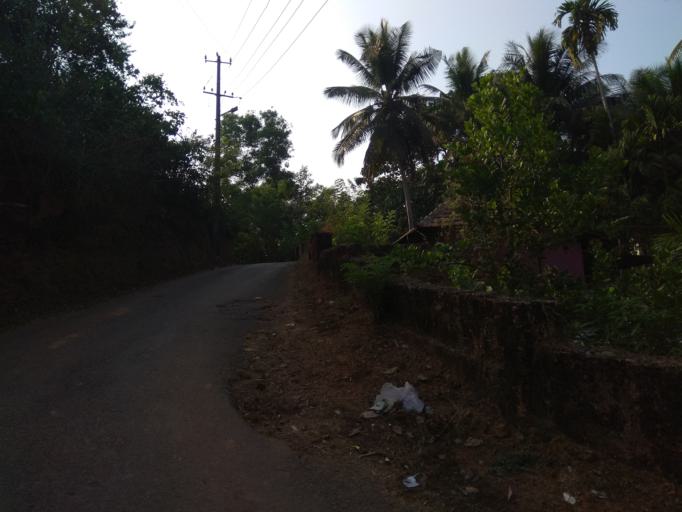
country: IN
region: Karnataka
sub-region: Dakshina Kannada
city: Mangalore
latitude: 12.9230
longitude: 74.8728
